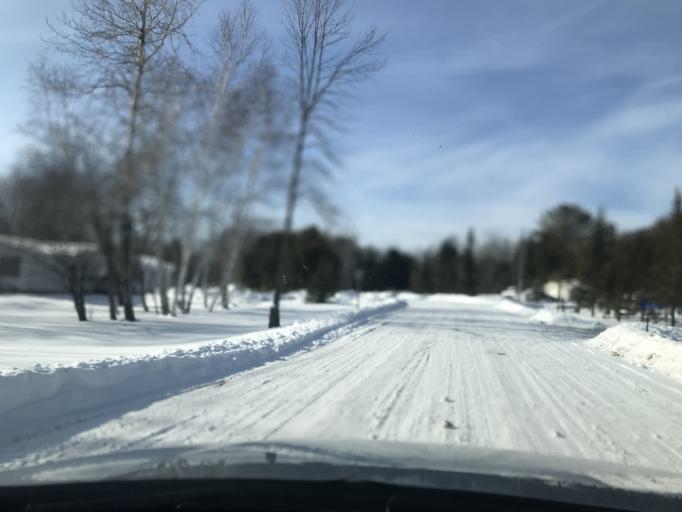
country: US
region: Wisconsin
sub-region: Oconto County
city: Gillett
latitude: 45.1504
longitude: -88.2207
